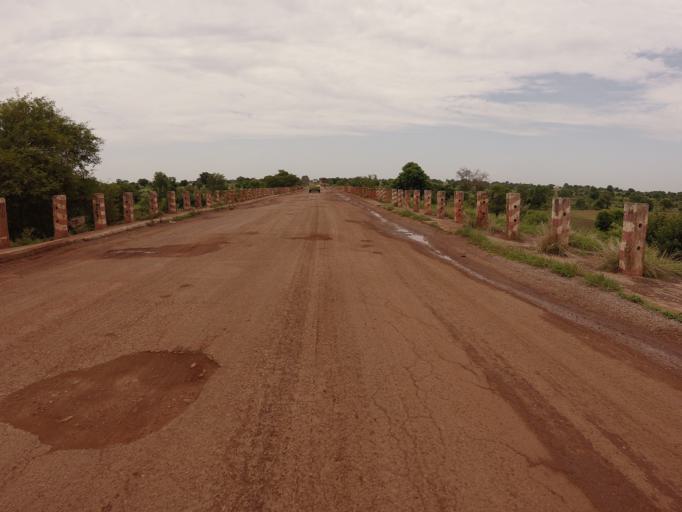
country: GH
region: Upper East
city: Bawku
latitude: 11.0025
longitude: -0.3828
